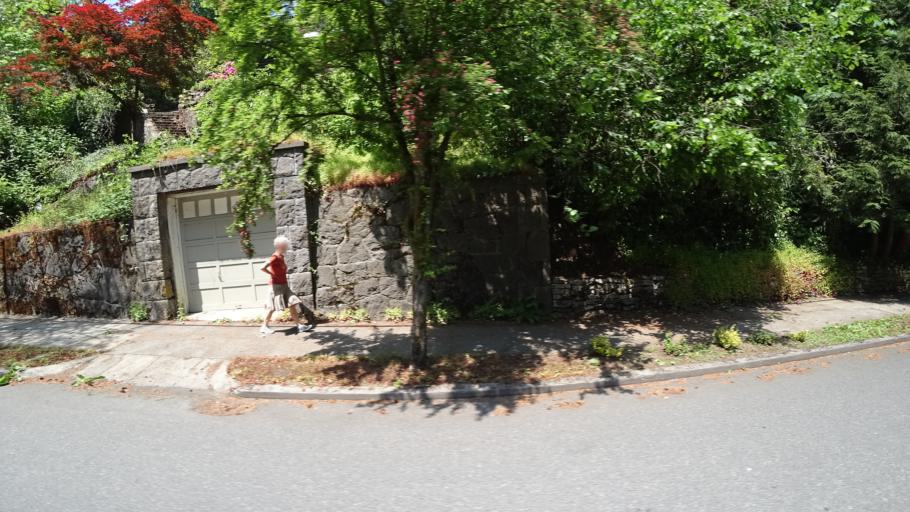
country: US
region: Oregon
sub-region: Multnomah County
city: Portland
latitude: 45.5200
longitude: -122.7097
